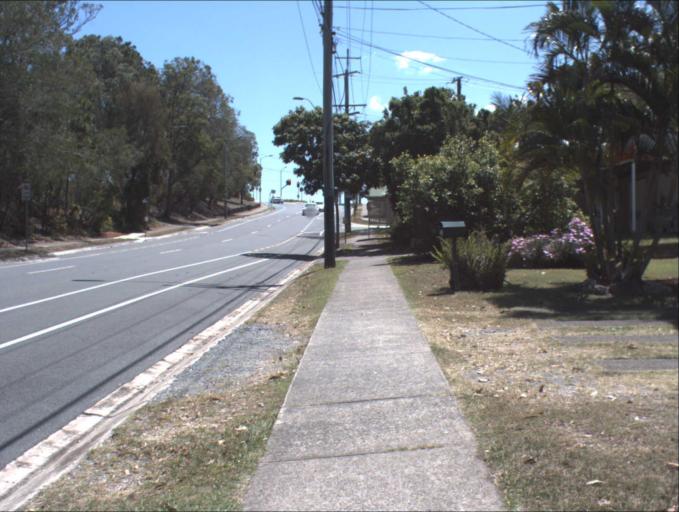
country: AU
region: Queensland
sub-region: Logan
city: Springwood
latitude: -27.6090
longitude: 153.1349
